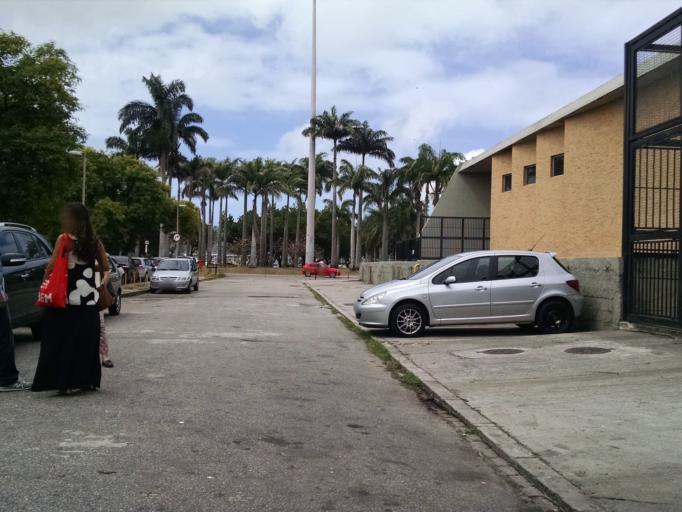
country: BR
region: Rio de Janeiro
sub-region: Rio De Janeiro
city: Rio de Janeiro
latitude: -22.9128
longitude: -43.1707
